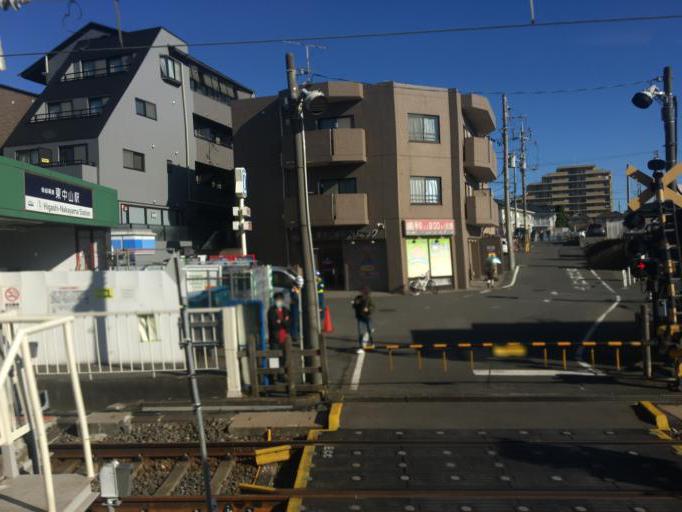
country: JP
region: Chiba
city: Funabashi
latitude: 35.7145
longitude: 139.9532
